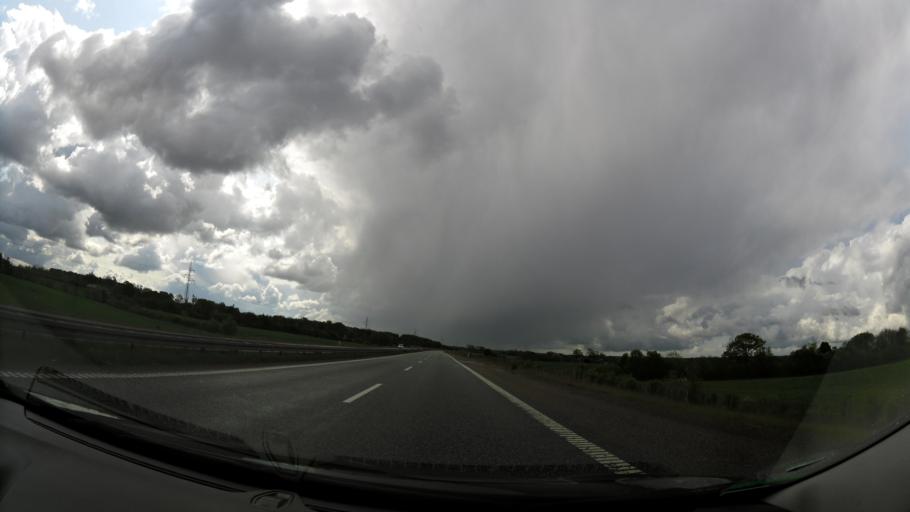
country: DK
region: South Denmark
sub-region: Svendborg Kommune
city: Svendborg
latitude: 55.1509
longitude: 10.5511
